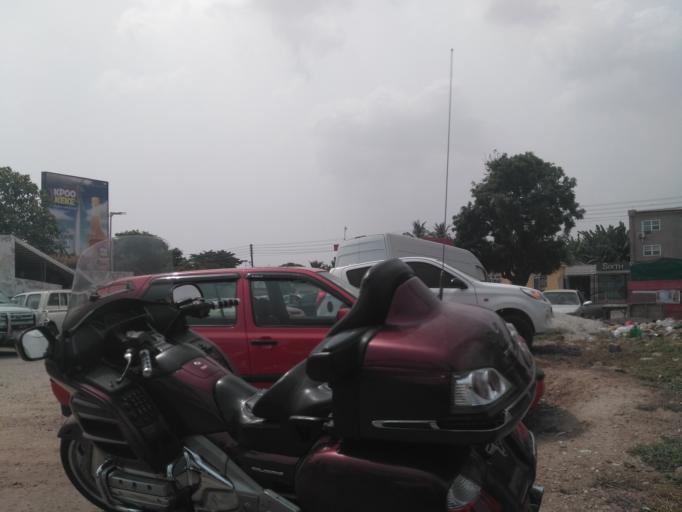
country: GH
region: Greater Accra
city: Accra
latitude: 5.5564
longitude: -0.1823
